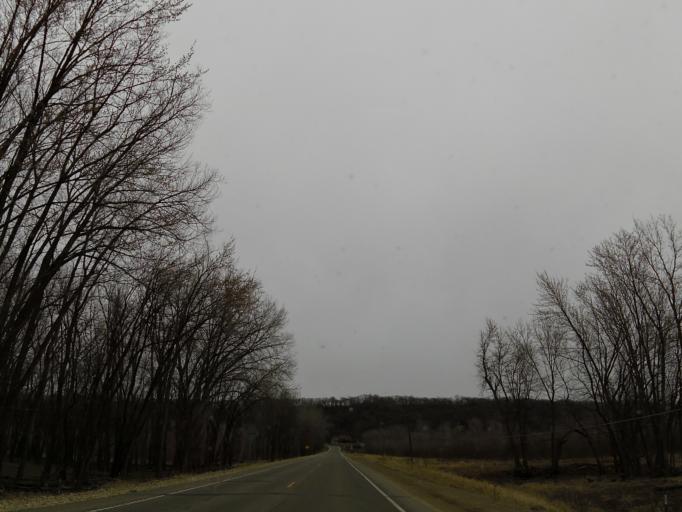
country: US
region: Minnesota
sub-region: Le Sueur County
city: Le Sueur
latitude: 44.5311
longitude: -93.8937
